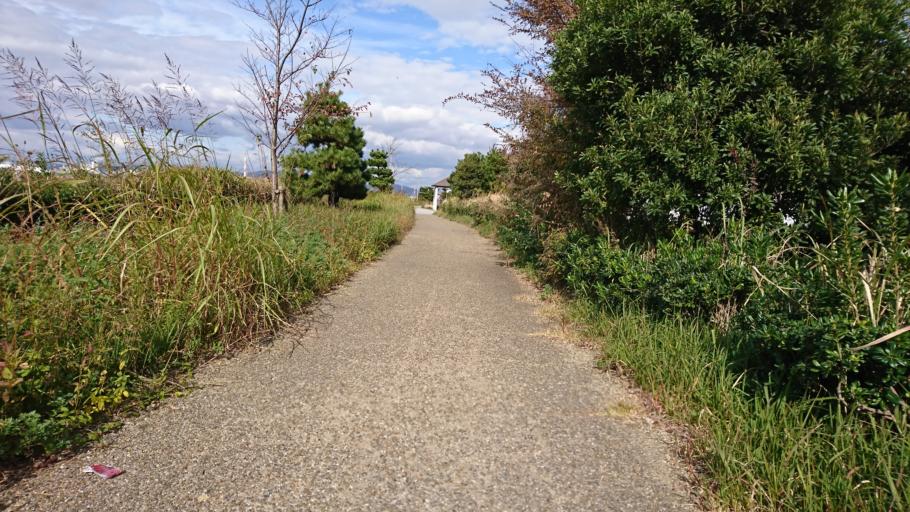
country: JP
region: Hyogo
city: Kakogawacho-honmachi
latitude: 34.7353
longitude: 134.8120
